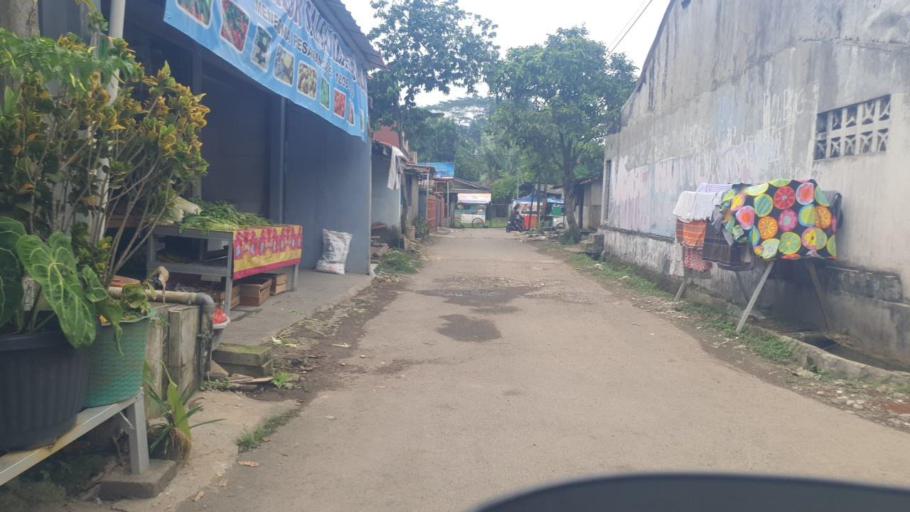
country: ID
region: West Java
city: Bogor
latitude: -6.5783
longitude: 106.7833
